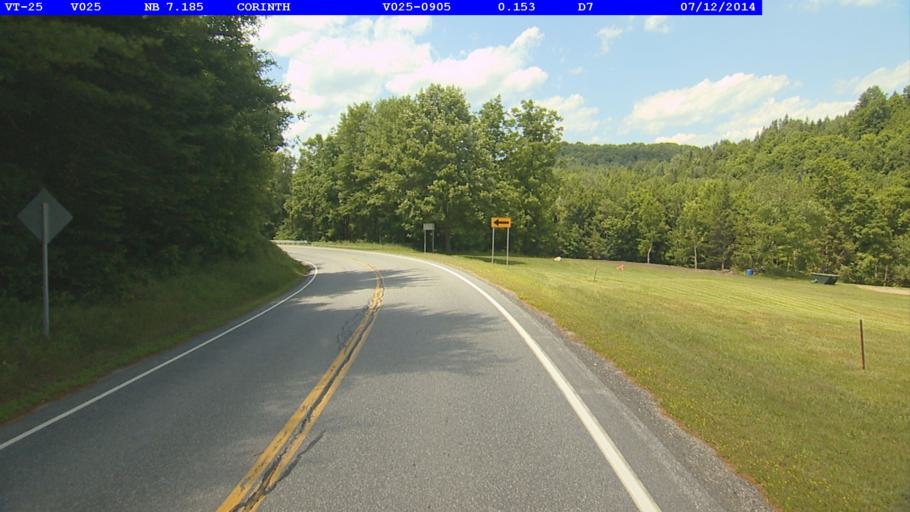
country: US
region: New Hampshire
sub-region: Grafton County
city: Haverhill
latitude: 44.0436
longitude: -72.2054
